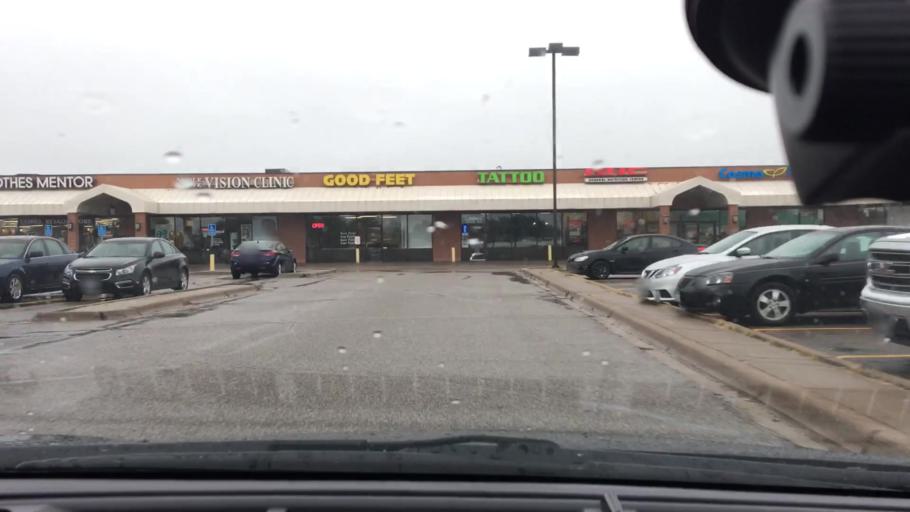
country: US
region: Minnesota
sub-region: Hennepin County
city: Maple Grove
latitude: 45.1029
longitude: -93.4541
